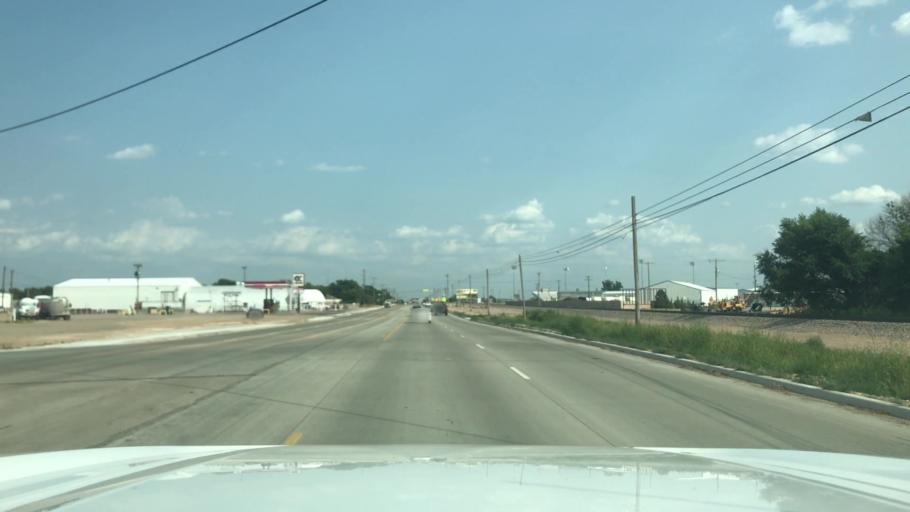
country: US
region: Texas
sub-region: Dallam County
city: Dalhart
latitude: 36.0541
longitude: -102.5054
